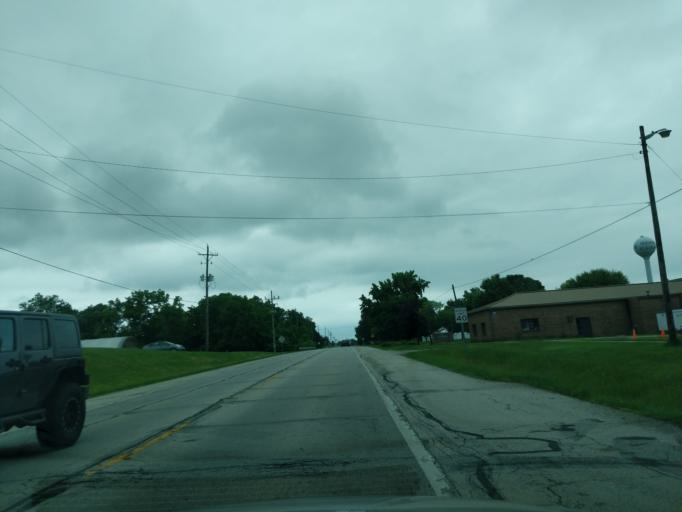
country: US
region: Indiana
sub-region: Hamilton County
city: Cicero
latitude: 40.1462
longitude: -86.0133
